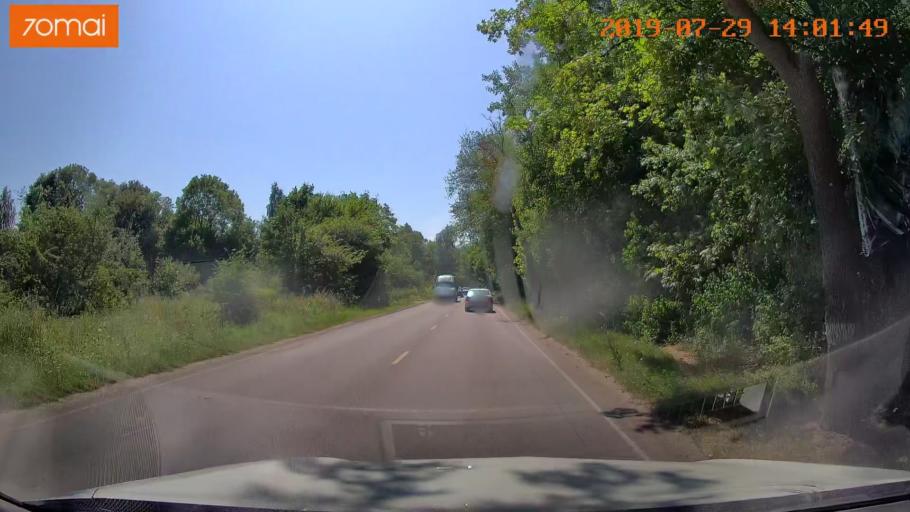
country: RU
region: Kaliningrad
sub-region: Gorod Kaliningrad
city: Baltiysk
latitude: 54.6675
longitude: 19.9192
